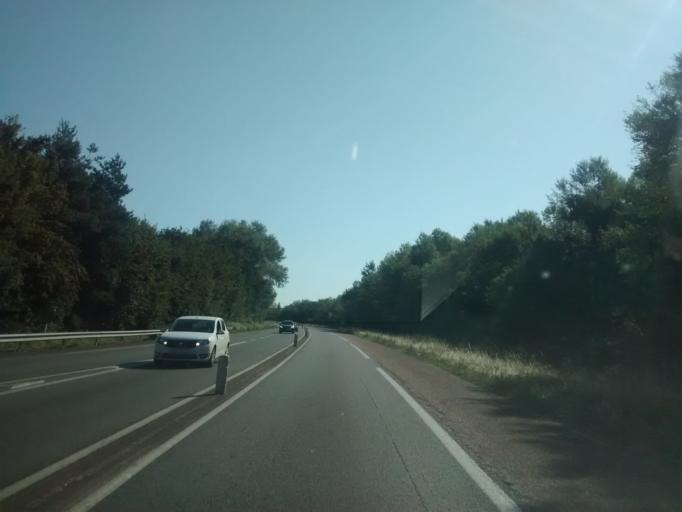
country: FR
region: Aquitaine
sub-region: Departement de la Gironde
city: Genissac
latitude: 44.8682
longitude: -0.2423
